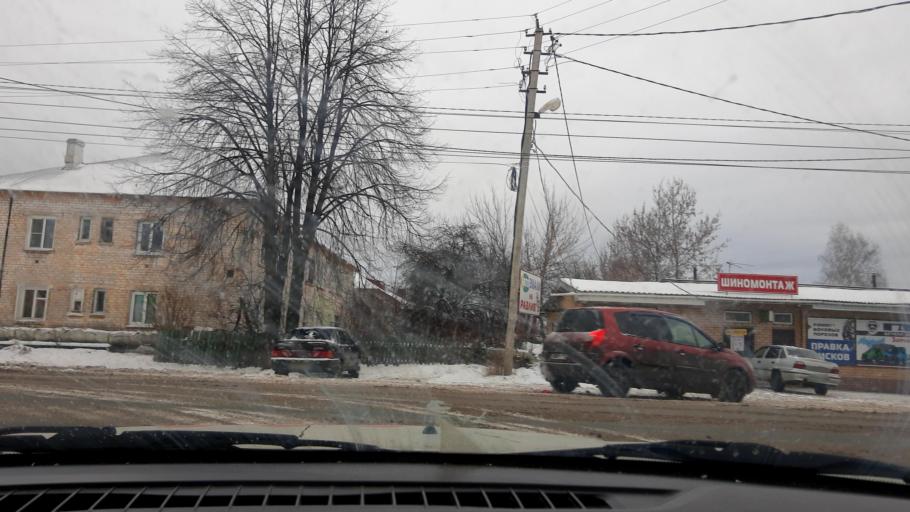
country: RU
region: Nizjnij Novgorod
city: Gorodets
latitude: 56.6561
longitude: 43.4870
